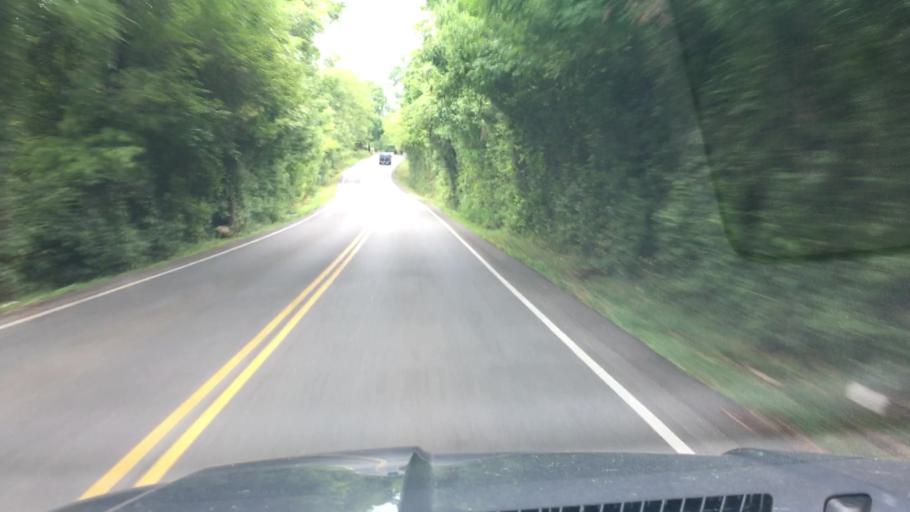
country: US
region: Tennessee
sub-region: Williamson County
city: Thompson's Station
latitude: 35.8037
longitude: -86.8628
